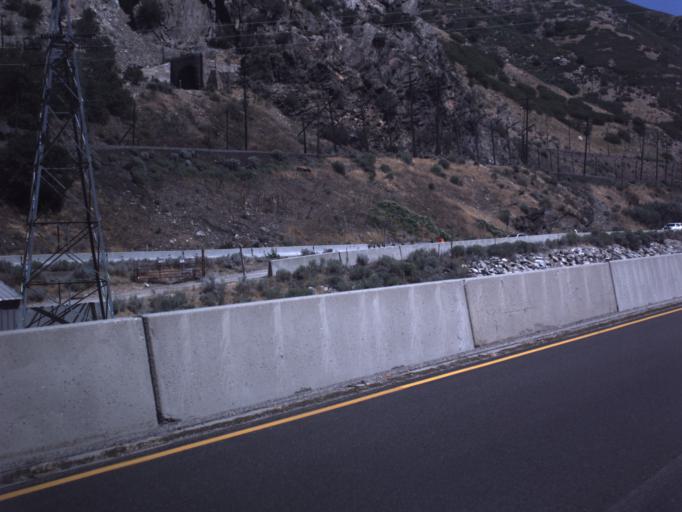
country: US
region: Utah
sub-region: Weber County
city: Uintah
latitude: 41.1371
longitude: -111.8825
